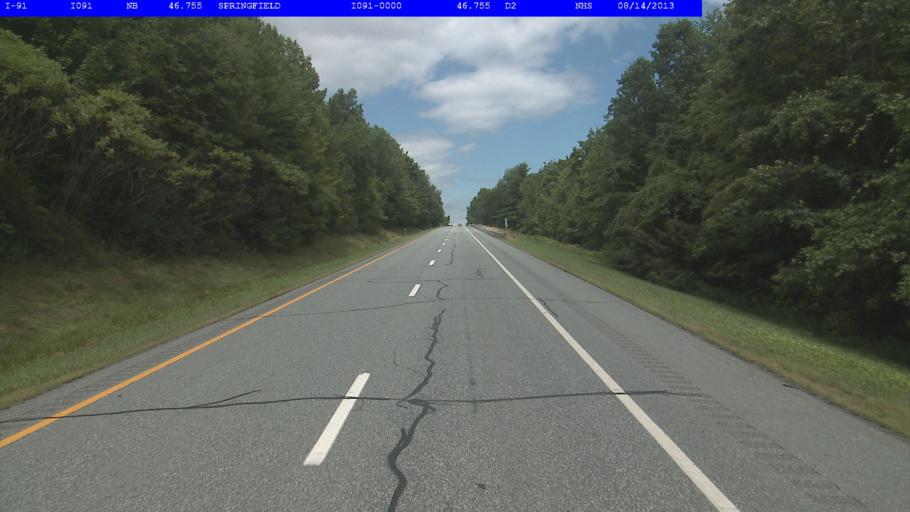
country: US
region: Vermont
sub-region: Windsor County
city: Springfield
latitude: 43.3379
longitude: -72.4196
